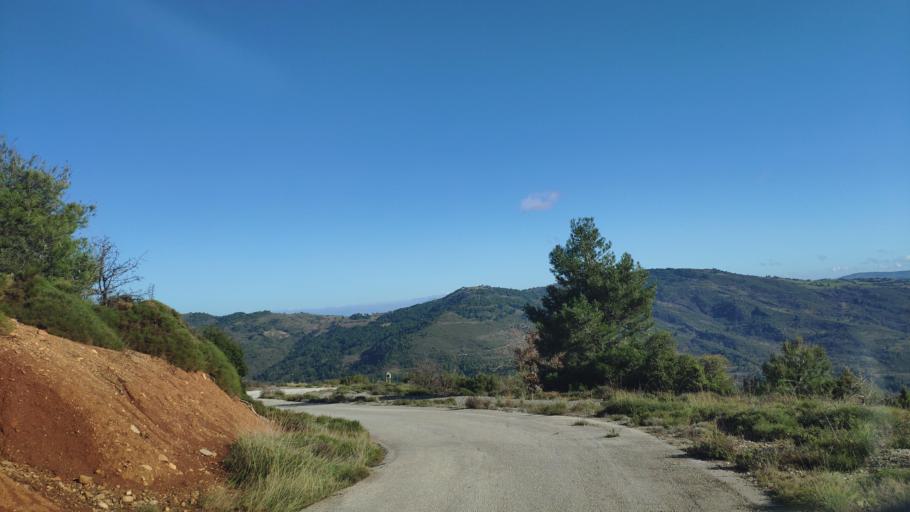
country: GR
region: West Greece
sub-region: Nomos Achaias
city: Aiyira
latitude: 38.0600
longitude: 22.4533
